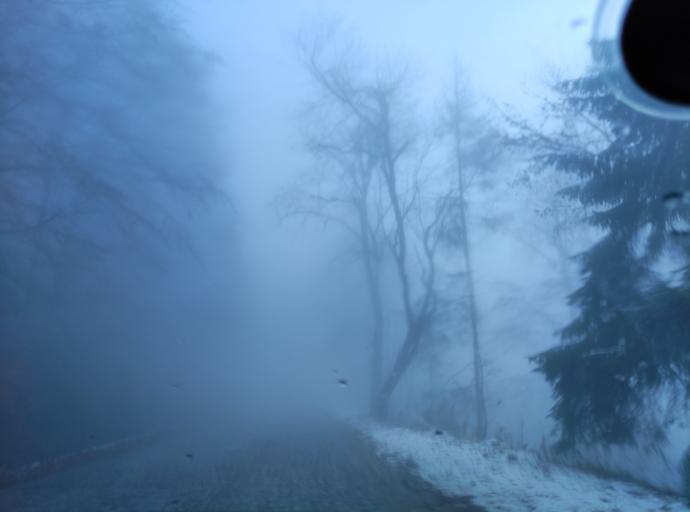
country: BG
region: Sofia-Capital
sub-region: Stolichna Obshtina
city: Sofia
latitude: 42.6126
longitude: 23.2960
